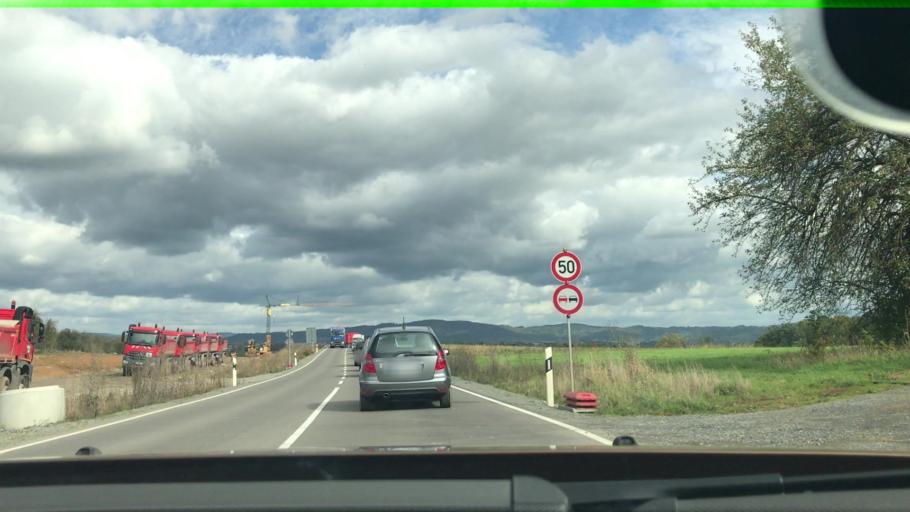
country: DE
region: Baden-Wuerttemberg
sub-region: Regierungsbezirk Stuttgart
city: Leutenbach
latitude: 48.9070
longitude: 9.4248
